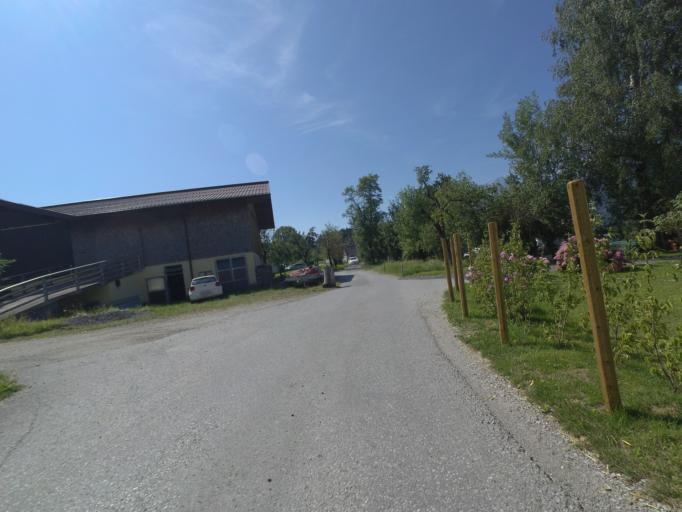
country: AT
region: Salzburg
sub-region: Politischer Bezirk Hallein
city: Adnet
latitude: 47.6723
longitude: 13.1406
